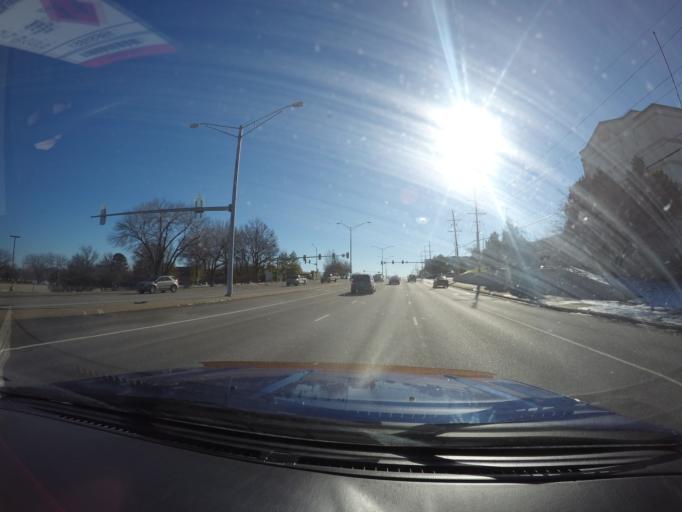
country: US
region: Kansas
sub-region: Johnson County
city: Leawood
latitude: 38.9302
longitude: -94.6490
